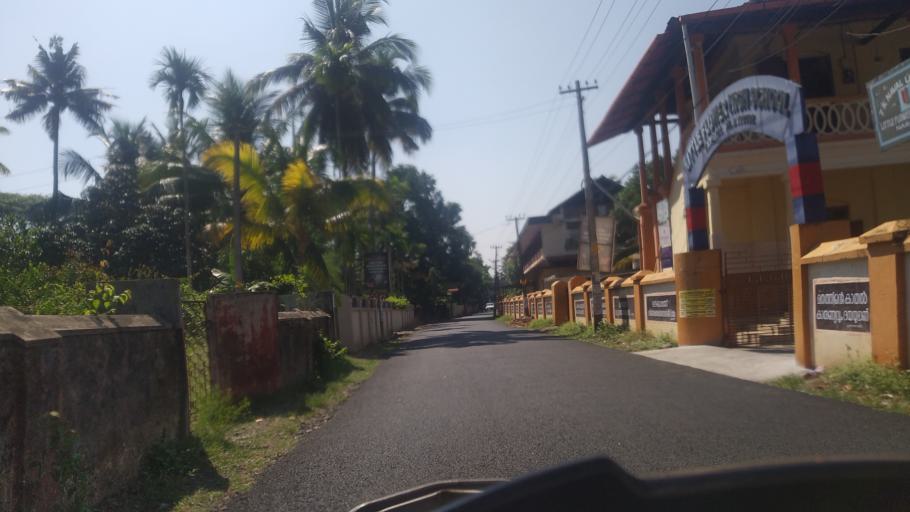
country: IN
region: Kerala
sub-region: Ernakulam
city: Elur
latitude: 10.0439
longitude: 76.2214
